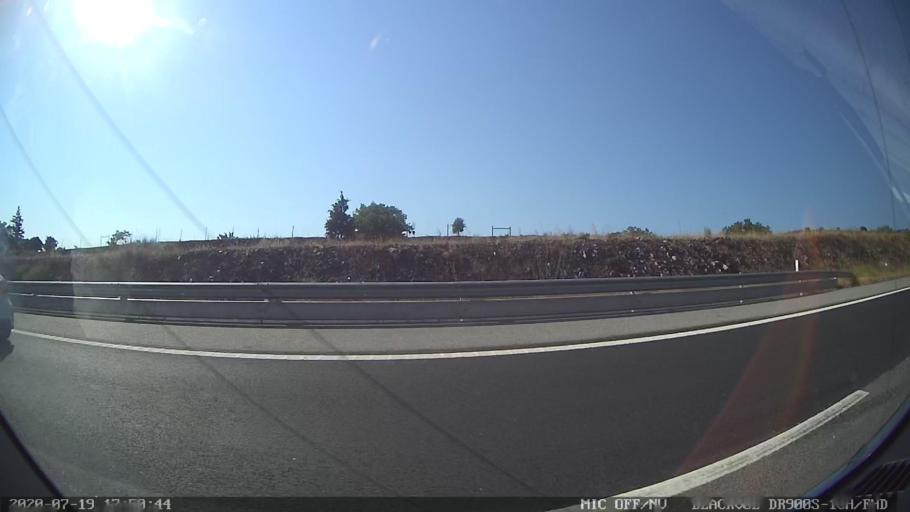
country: PT
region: Braganca
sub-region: Macedo de Cavaleiros
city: Macedo de Cavaleiros
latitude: 41.5655
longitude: -7.0087
